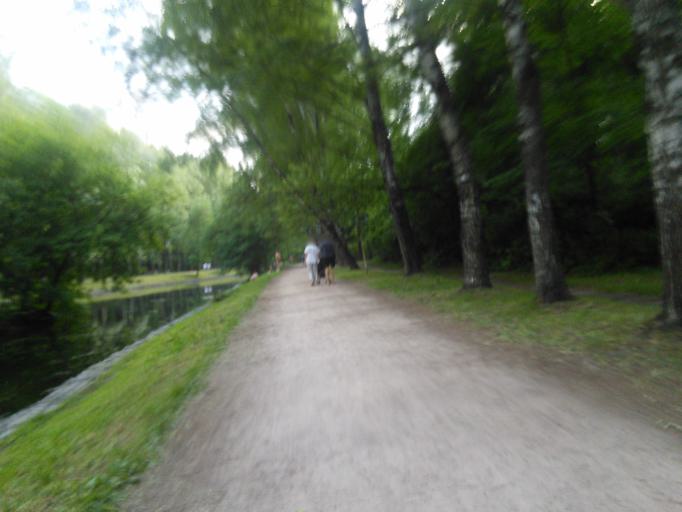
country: RU
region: Moscow
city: Sokol'niki
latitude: 55.8131
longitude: 37.6703
